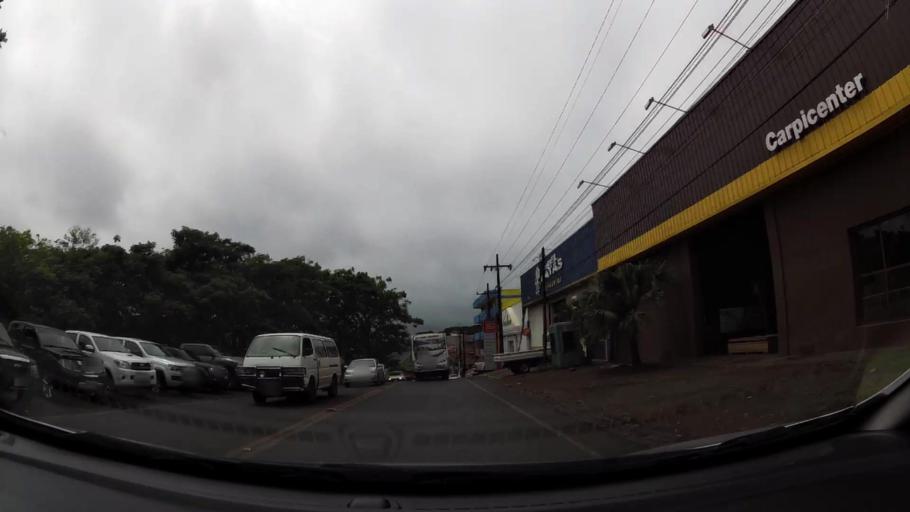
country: PY
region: Alto Parana
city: Ciudad del Este
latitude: -25.5025
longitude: -54.6539
